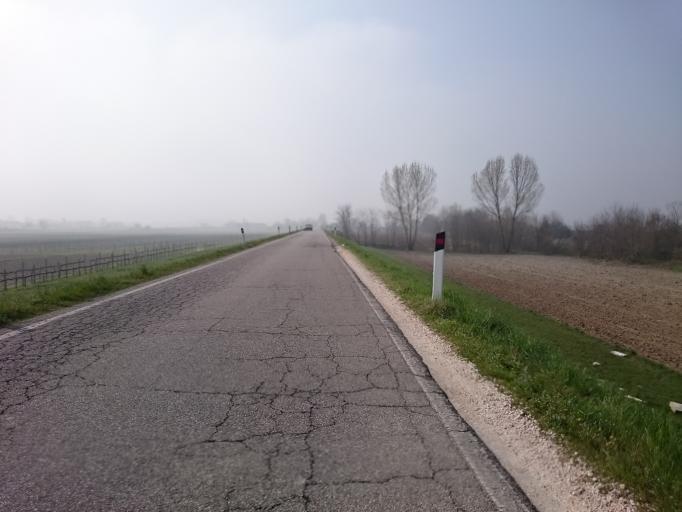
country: IT
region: Veneto
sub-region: Provincia di Padova
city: Due Carrare
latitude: 45.2789
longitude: 11.8310
